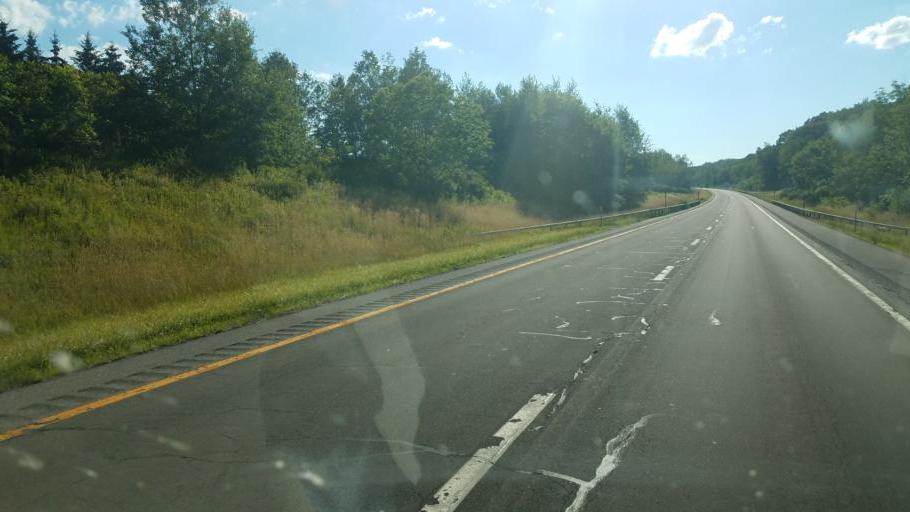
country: US
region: New York
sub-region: Chautauqua County
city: Falconer
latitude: 42.1371
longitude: -79.1547
